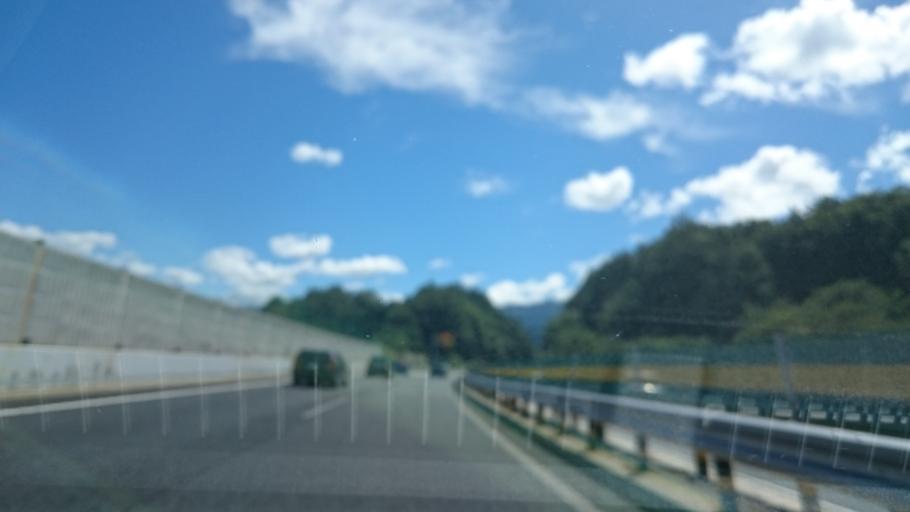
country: JP
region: Nagano
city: Iida
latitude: 35.4601
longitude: 137.7526
